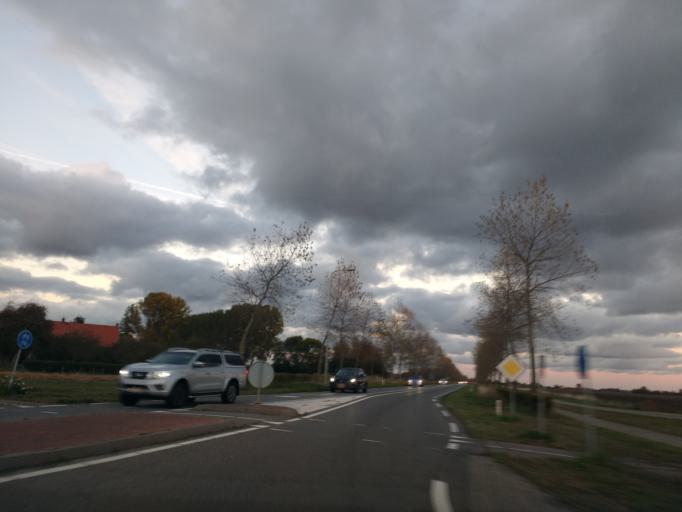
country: NL
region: Zeeland
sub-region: Gemeente Sluis
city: Sluis
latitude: 51.3015
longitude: 3.4360
